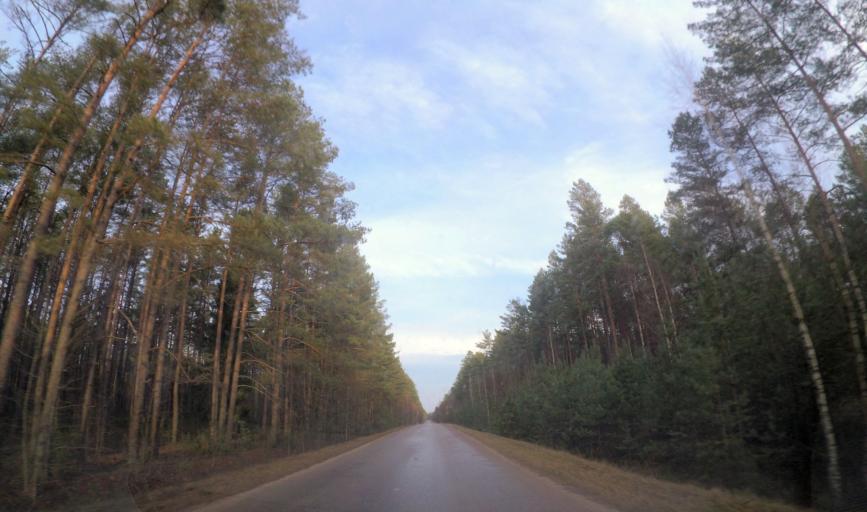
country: LT
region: Alytaus apskritis
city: Druskininkai
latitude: 53.9019
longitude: 24.1491
